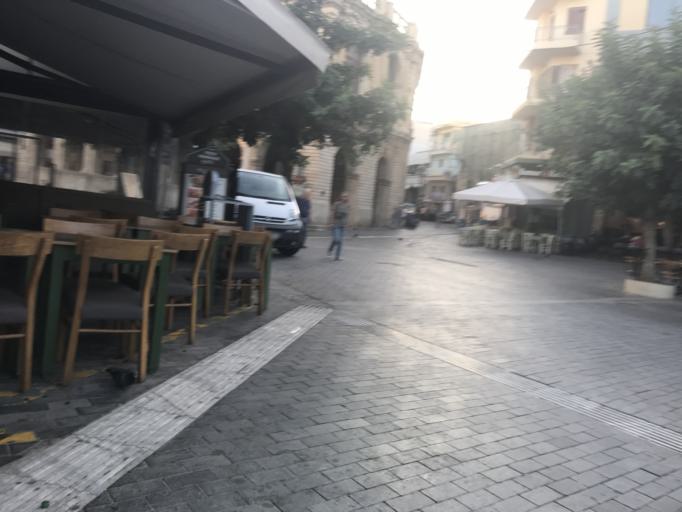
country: GR
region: Crete
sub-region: Nomos Irakleiou
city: Irakleion
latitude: 35.3396
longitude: 25.1336
